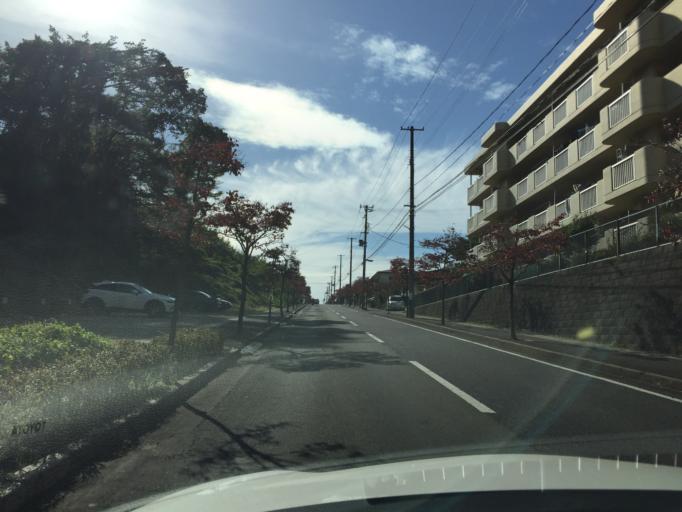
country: JP
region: Fukushima
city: Miharu
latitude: 37.4471
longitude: 140.4837
